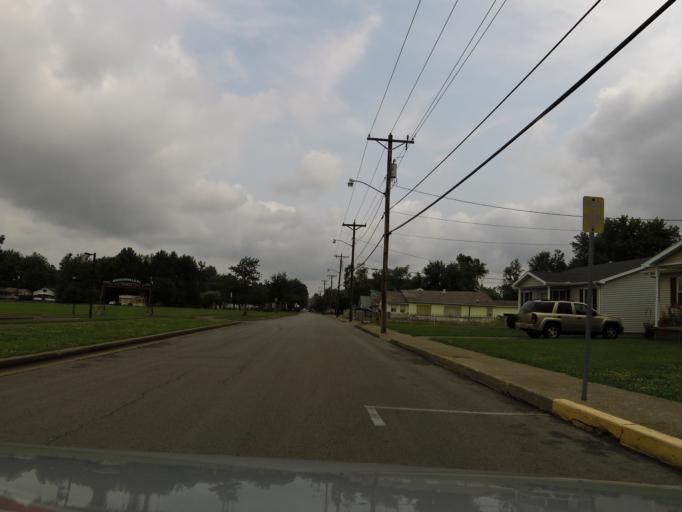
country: US
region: Kentucky
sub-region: Hopkins County
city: Madisonville
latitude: 37.3366
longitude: -87.5022
